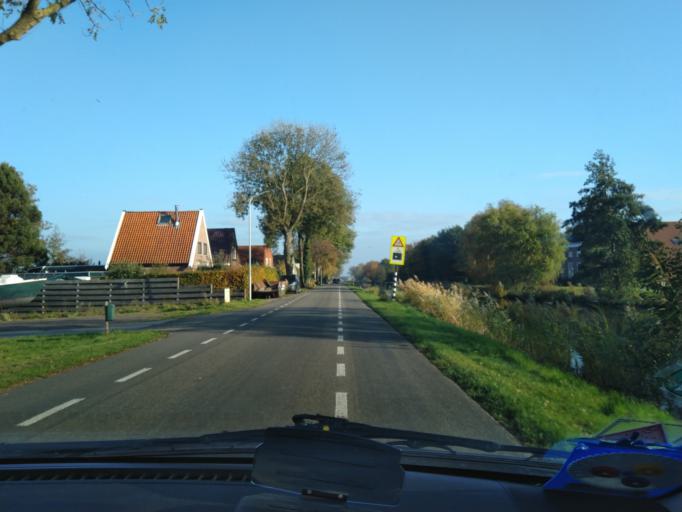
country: NL
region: Groningen
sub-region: Gemeente Hoogezand-Sappemeer
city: Sappemeer
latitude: 53.1638
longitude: 6.8184
